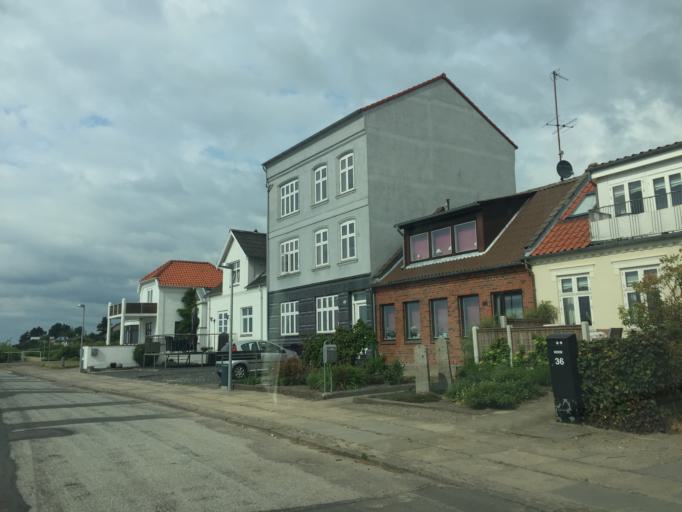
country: DK
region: South Denmark
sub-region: Assens Kommune
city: Assens
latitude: 55.2733
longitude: 9.8907
